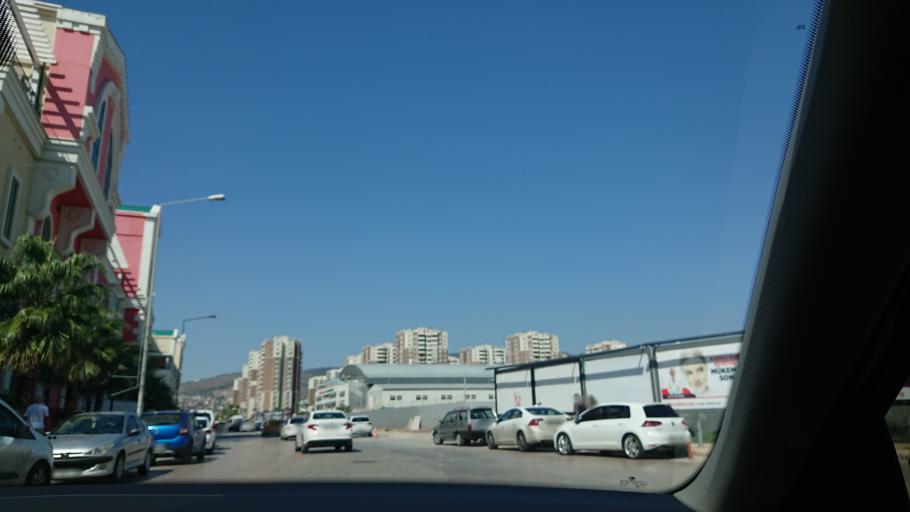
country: TR
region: Izmir
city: Karsiyaka
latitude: 38.4724
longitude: 27.0757
